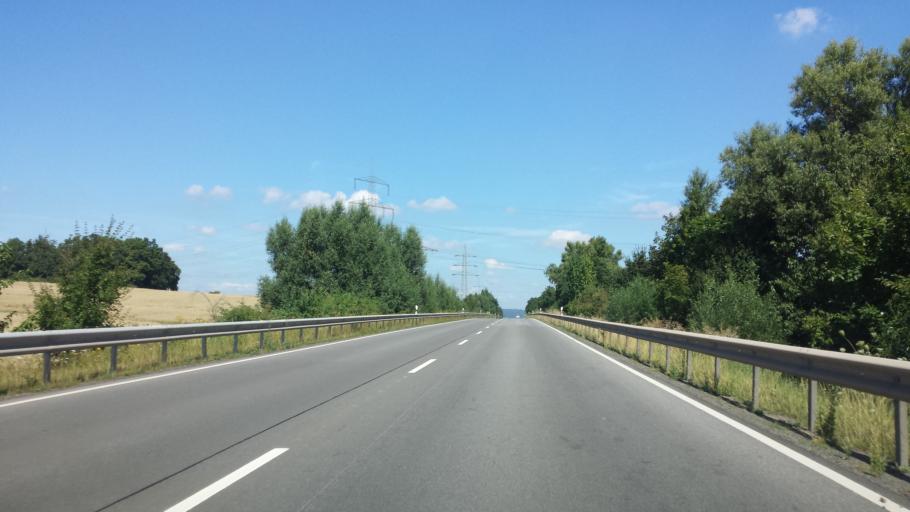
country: DE
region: Rheinland-Pfalz
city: Gollheim
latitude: 49.5824
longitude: 8.0463
